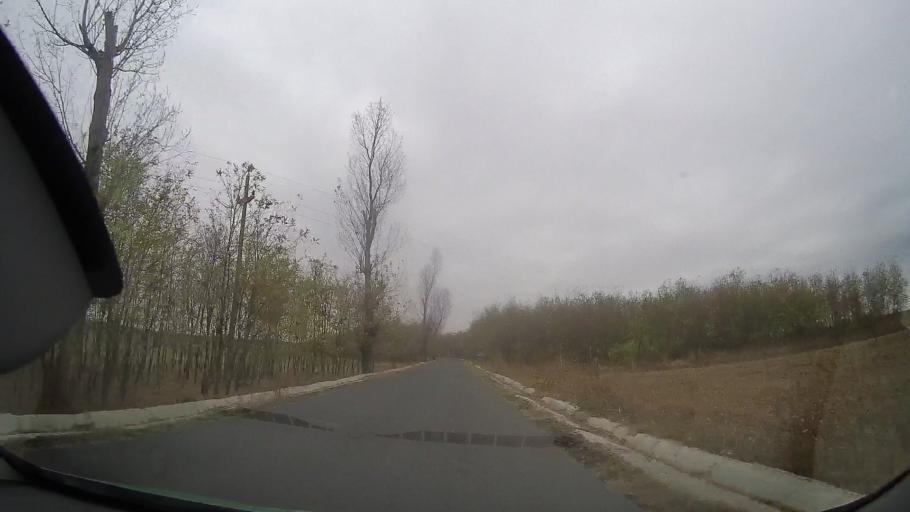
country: RO
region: Braila
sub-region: Comuna Ciocile
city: Ciocile
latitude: 44.7959
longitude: 27.2756
